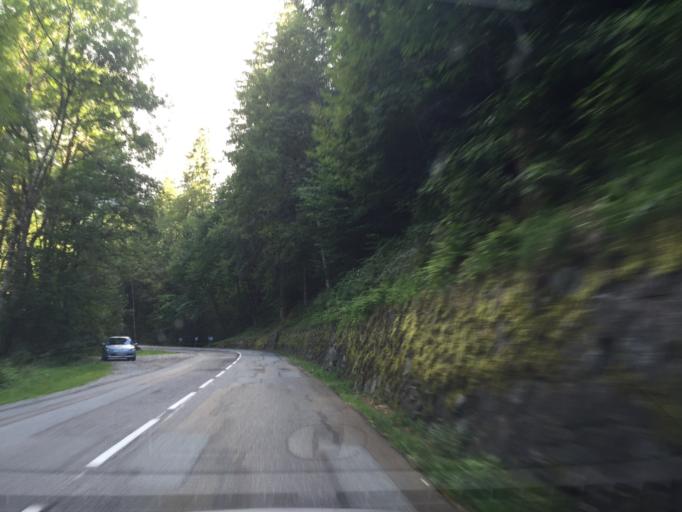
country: FR
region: Rhone-Alpes
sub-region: Departement de la Savoie
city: La Rochette
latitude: 45.4652
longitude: 6.1746
